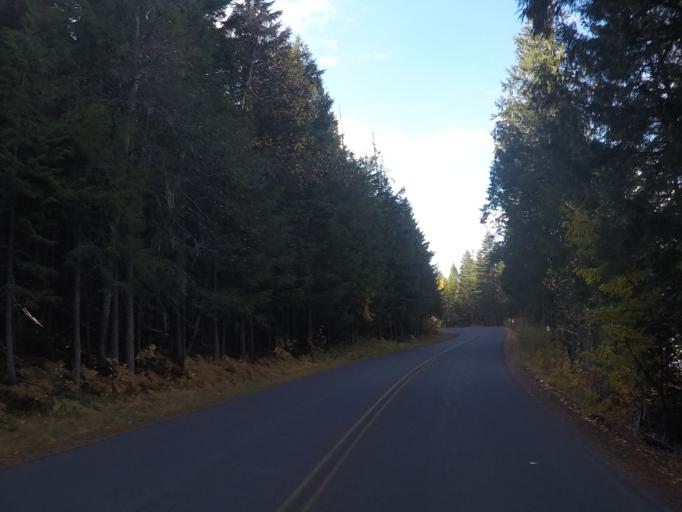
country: US
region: Montana
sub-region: Flathead County
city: Columbia Falls
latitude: 48.5770
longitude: -113.9060
